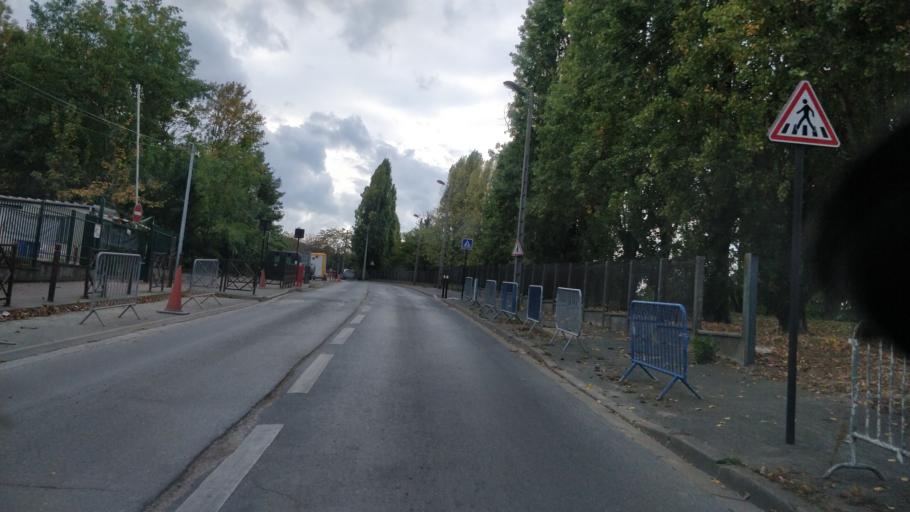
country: FR
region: Ile-de-France
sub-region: Departement de Seine-Saint-Denis
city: Livry-Gargan
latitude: 48.9236
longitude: 2.5509
